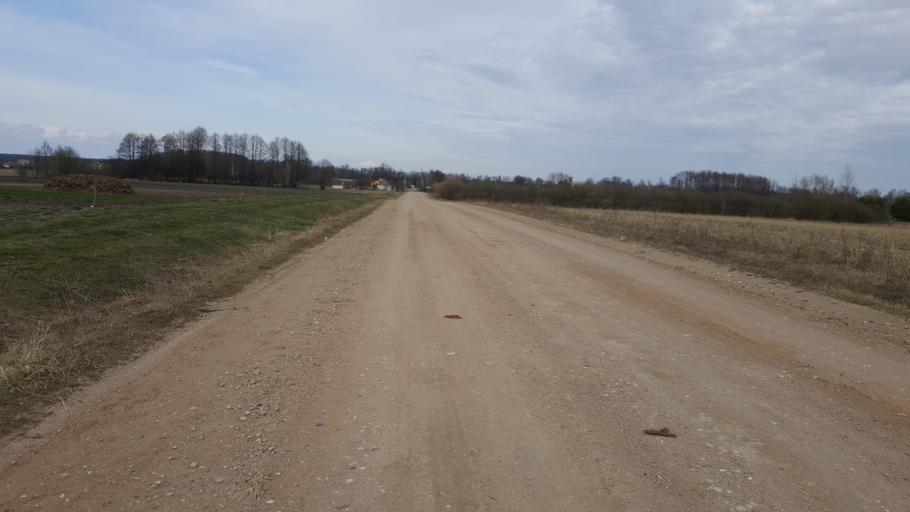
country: BY
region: Brest
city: Kamyanyets
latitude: 52.3877
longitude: 23.9981
